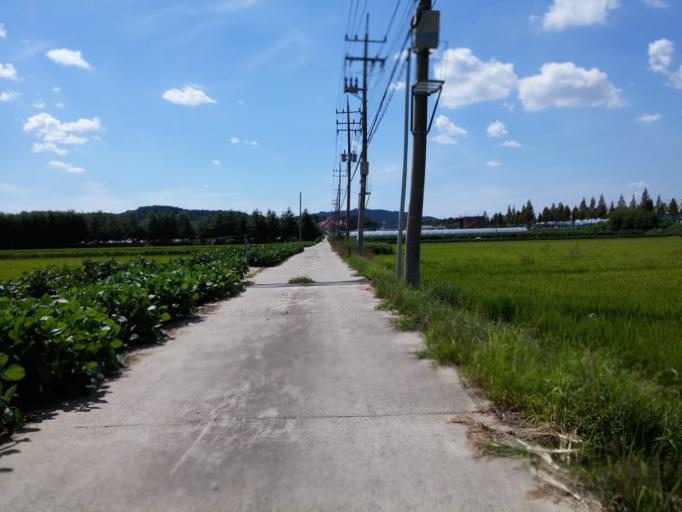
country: KR
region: Chungcheongbuk-do
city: Cheongju-si
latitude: 36.5948
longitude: 127.4960
